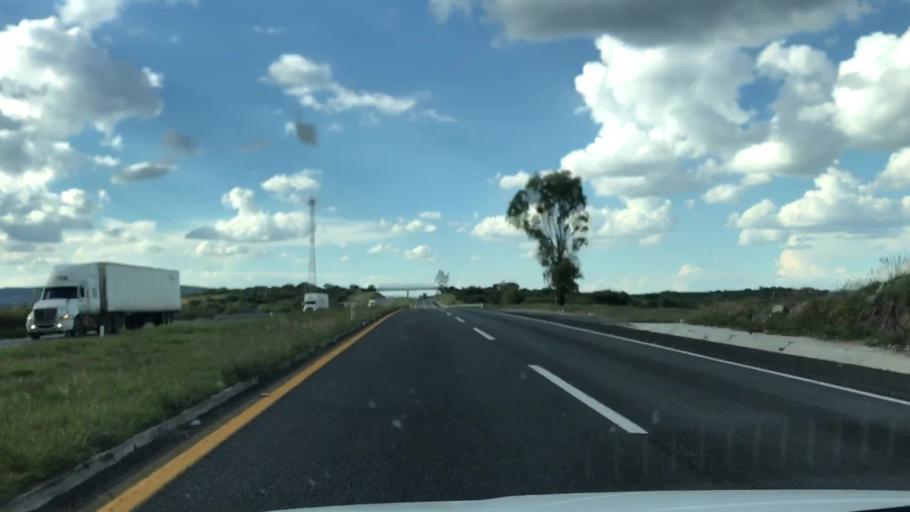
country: MX
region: Jalisco
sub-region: Union de San Antonio
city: San Jose del Caliche (El Caliche)
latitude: 21.2068
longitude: -101.9070
